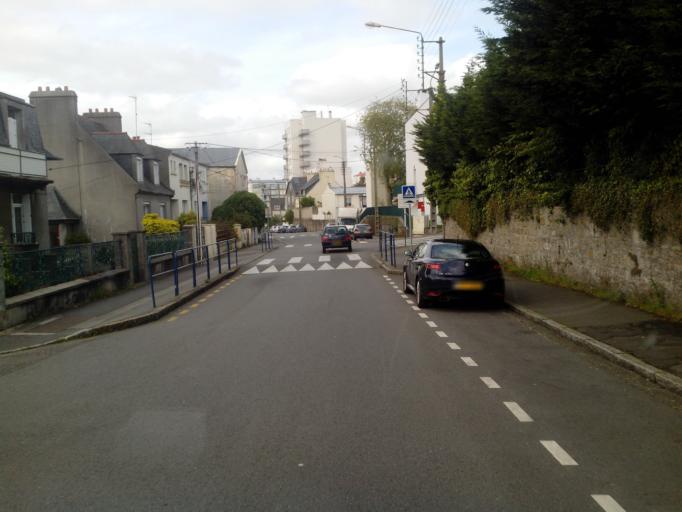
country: FR
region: Brittany
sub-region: Departement du Finistere
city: Brest
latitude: 48.4030
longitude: -4.4784
